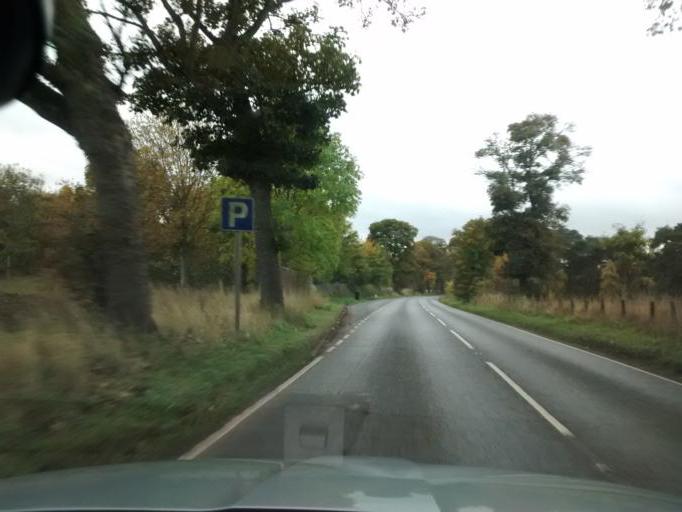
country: GB
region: Scotland
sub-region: Perth and Kinross
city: Blairgowrie
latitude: 56.5528
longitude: -3.3500
